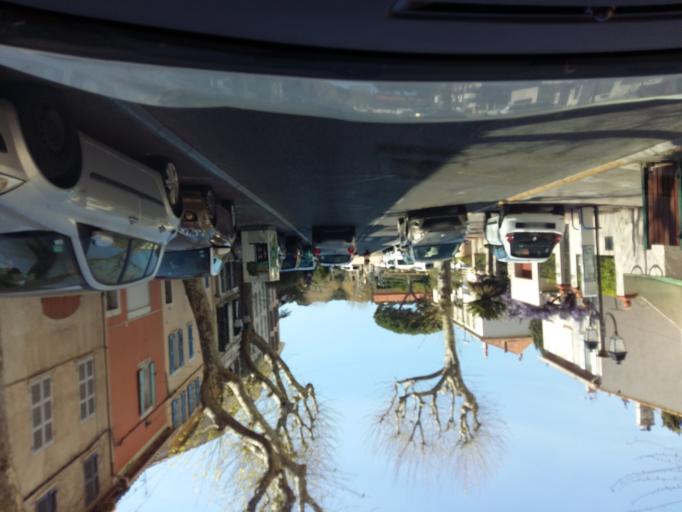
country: FR
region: Provence-Alpes-Cote d'Azur
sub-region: Departement du Var
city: Ollioules
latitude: 43.1373
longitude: 5.8502
